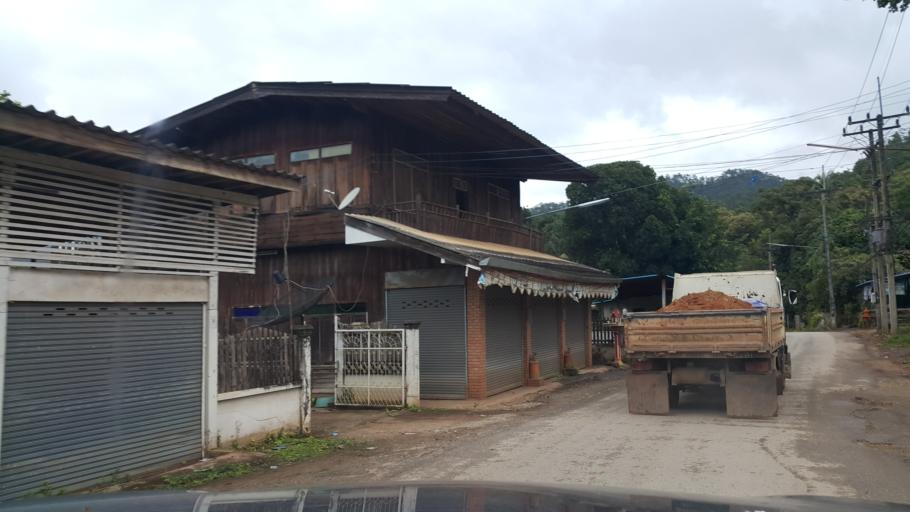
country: TH
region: Chiang Mai
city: Samoeng
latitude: 18.8581
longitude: 98.7311
